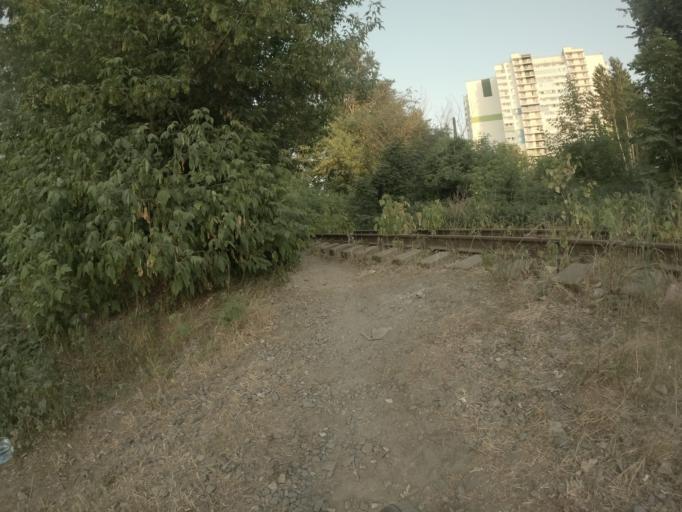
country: RU
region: St.-Petersburg
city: Krasnogvargeisky
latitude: 59.9411
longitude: 30.4384
